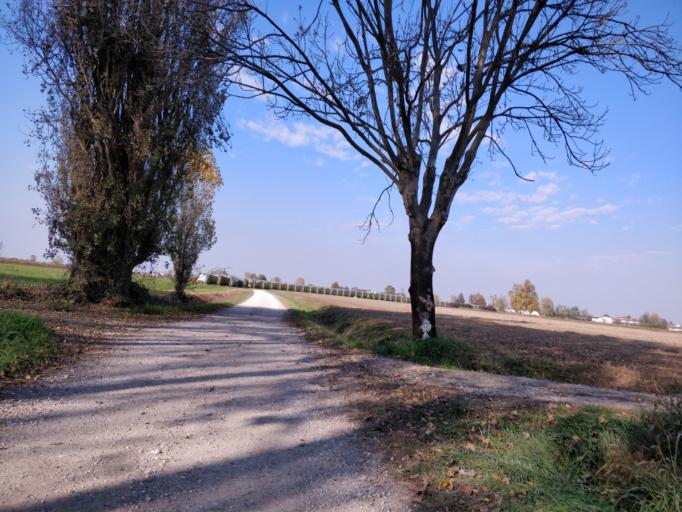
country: IT
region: Friuli Venezia Giulia
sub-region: Provincia di Udine
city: Bertiolo
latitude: 45.9343
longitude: 13.0411
